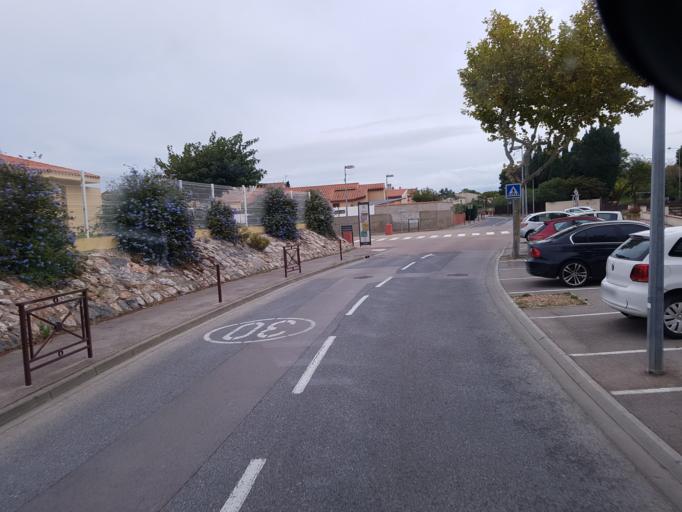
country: FR
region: Languedoc-Roussillon
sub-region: Departement des Pyrenees-Orientales
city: Torreilles
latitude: 42.7561
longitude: 2.9938
